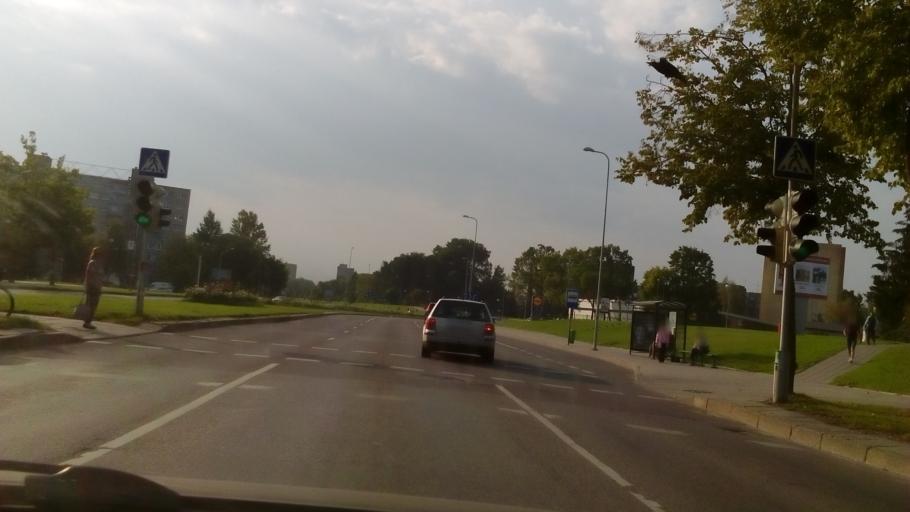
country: LT
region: Alytaus apskritis
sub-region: Alytus
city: Alytus
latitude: 54.4018
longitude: 24.0224
